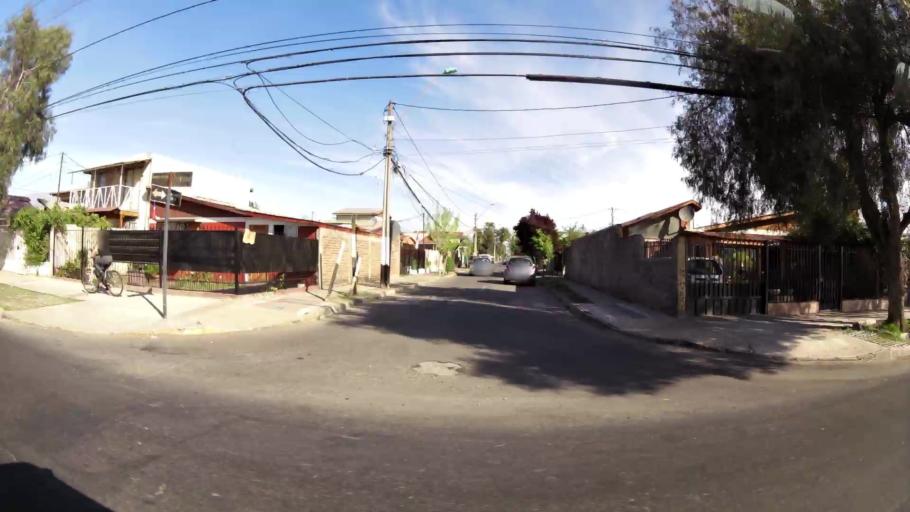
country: CL
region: Santiago Metropolitan
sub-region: Provincia de Cordillera
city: Puente Alto
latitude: -33.6060
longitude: -70.5998
